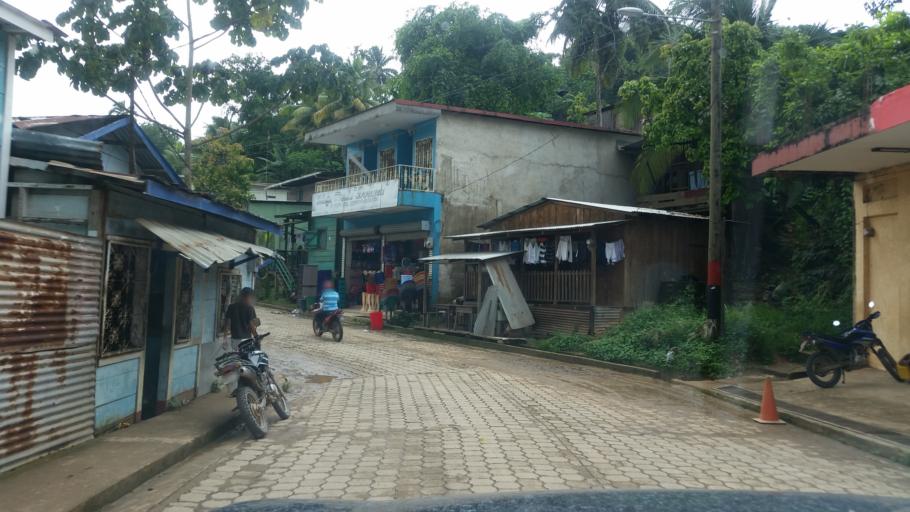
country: NI
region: Atlantico Norte (RAAN)
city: Bonanza
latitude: 14.0310
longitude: -84.5993
